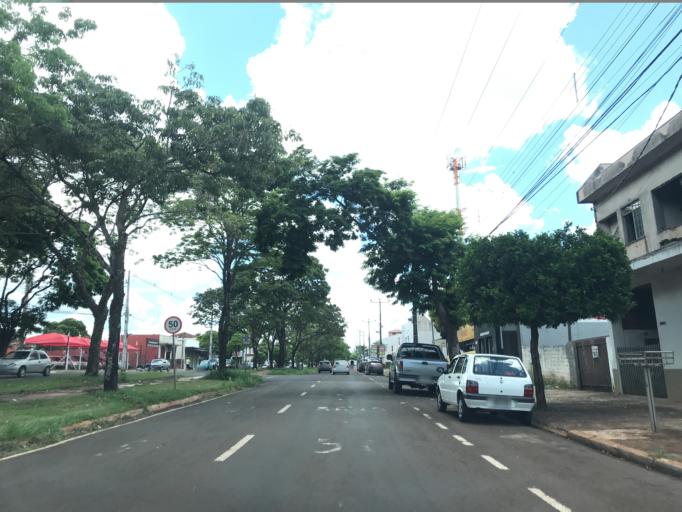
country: BR
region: Parana
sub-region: Maringa
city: Maringa
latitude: -23.3913
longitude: -51.9165
